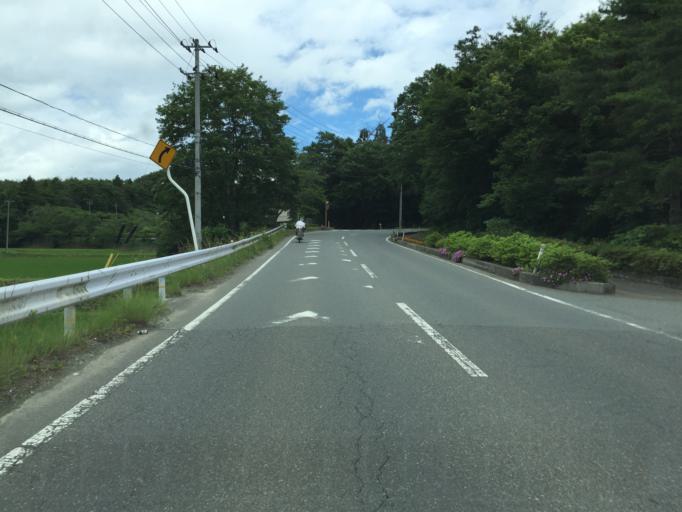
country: JP
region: Fukushima
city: Namie
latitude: 37.6675
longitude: 140.9613
